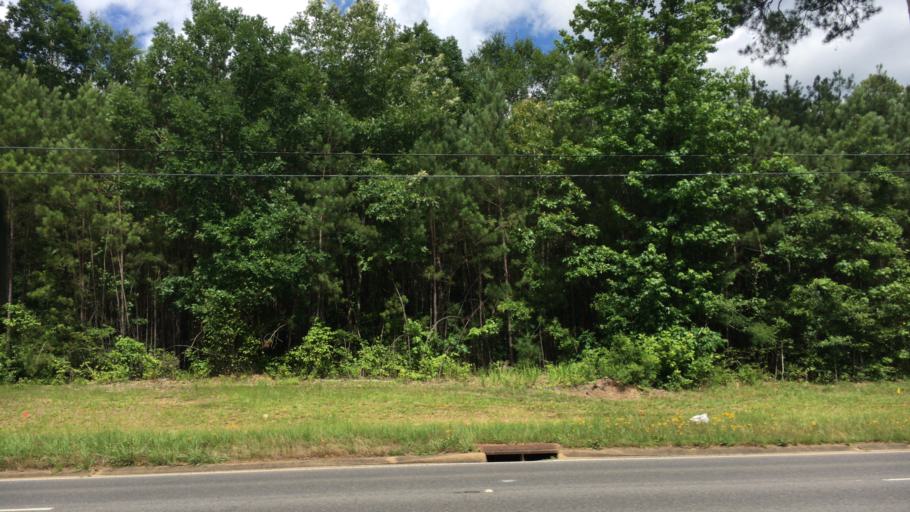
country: US
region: Louisiana
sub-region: Lincoln Parish
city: Ruston
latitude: 32.5014
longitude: -92.6369
